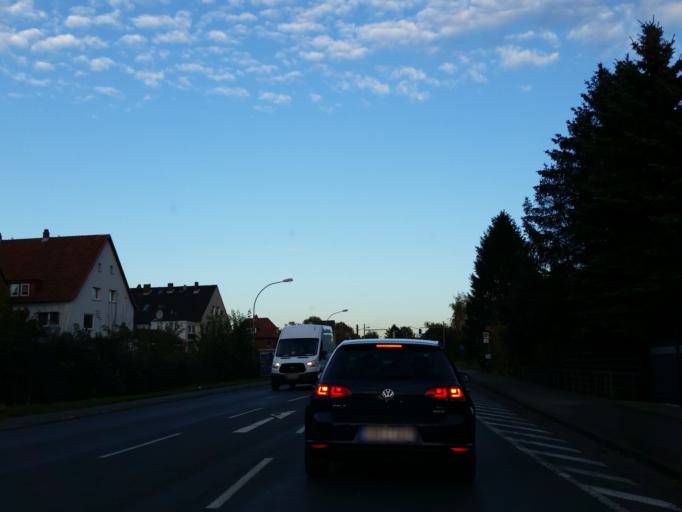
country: DE
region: Lower Saxony
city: Braunschweig
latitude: 52.2856
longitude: 10.5886
